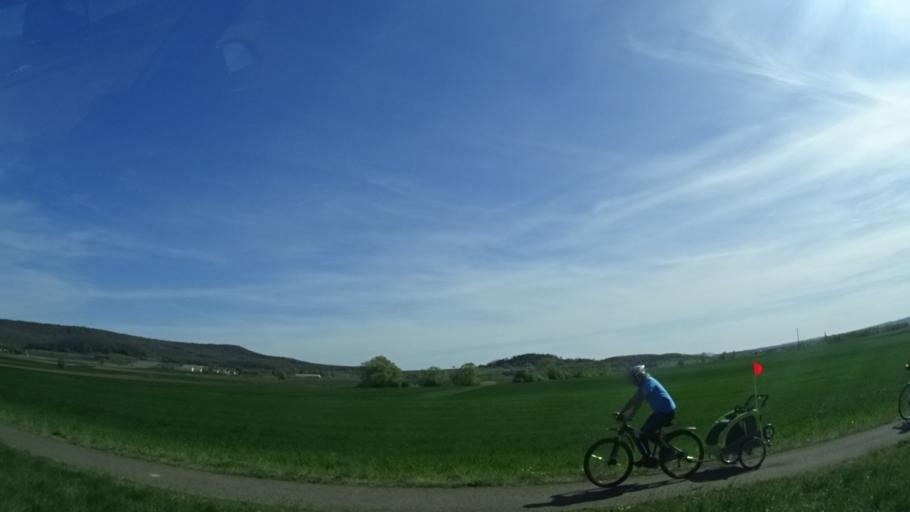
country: DE
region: Bavaria
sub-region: Regierungsbezirk Unterfranken
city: Hofheim in Unterfranken
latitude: 50.1383
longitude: 10.5475
